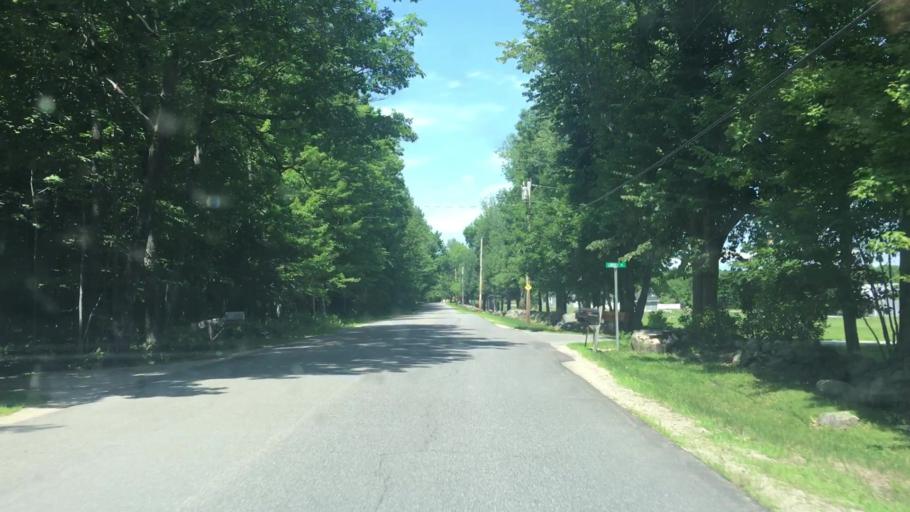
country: US
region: Maine
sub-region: Kennebec County
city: Monmouth
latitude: 44.2807
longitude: -70.0545
